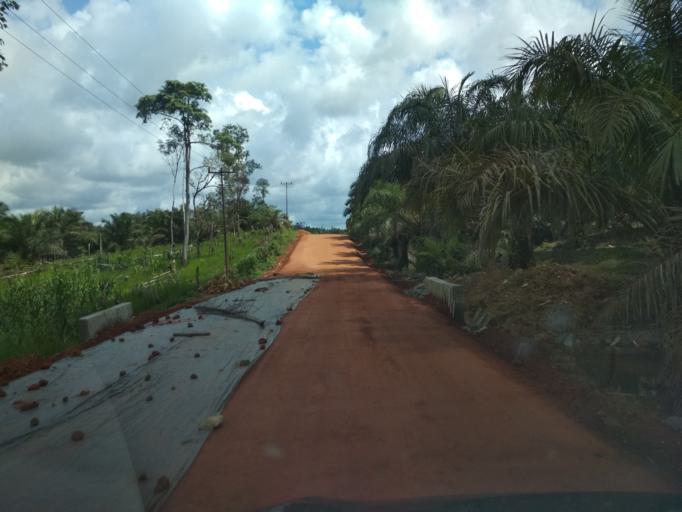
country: ID
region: West Kalimantan
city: Tayan
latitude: 0.5429
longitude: 110.0899
